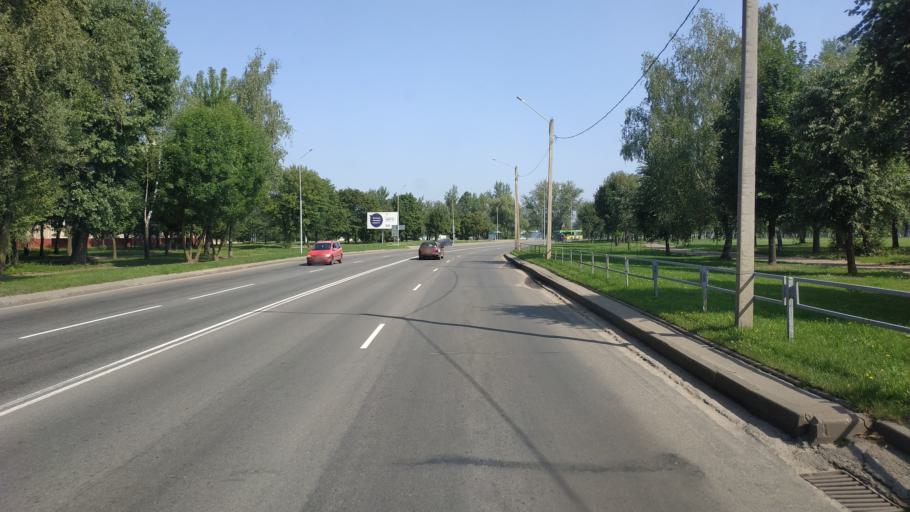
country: BY
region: Mogilev
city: Buynichy
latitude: 53.8739
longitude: 30.3125
